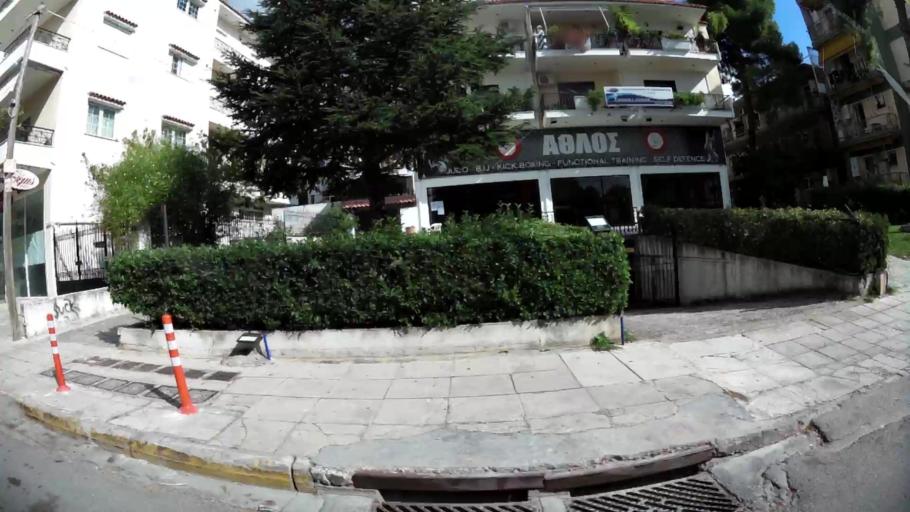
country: GR
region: Attica
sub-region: Nomarchia Athinas
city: Melissia
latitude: 38.0557
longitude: 23.8401
